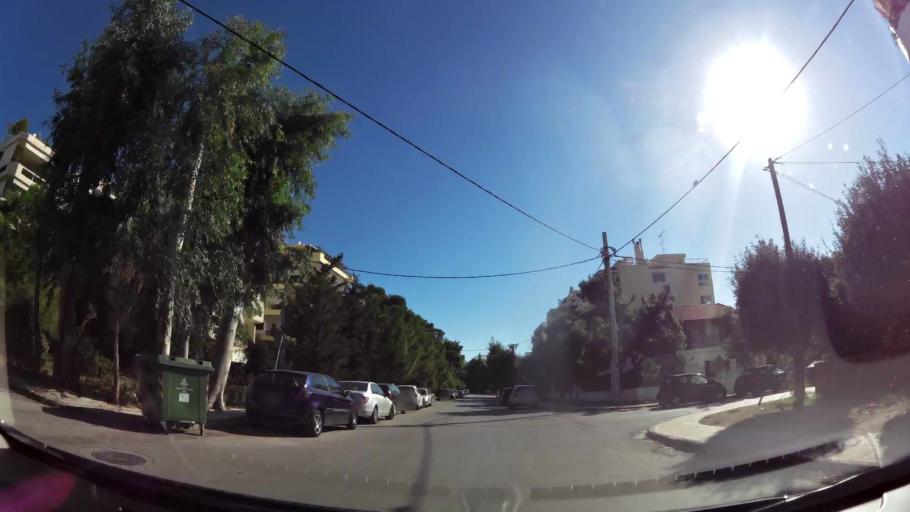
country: GR
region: Attica
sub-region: Nomarchia Athinas
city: Glyfada
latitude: 37.8529
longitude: 23.7653
